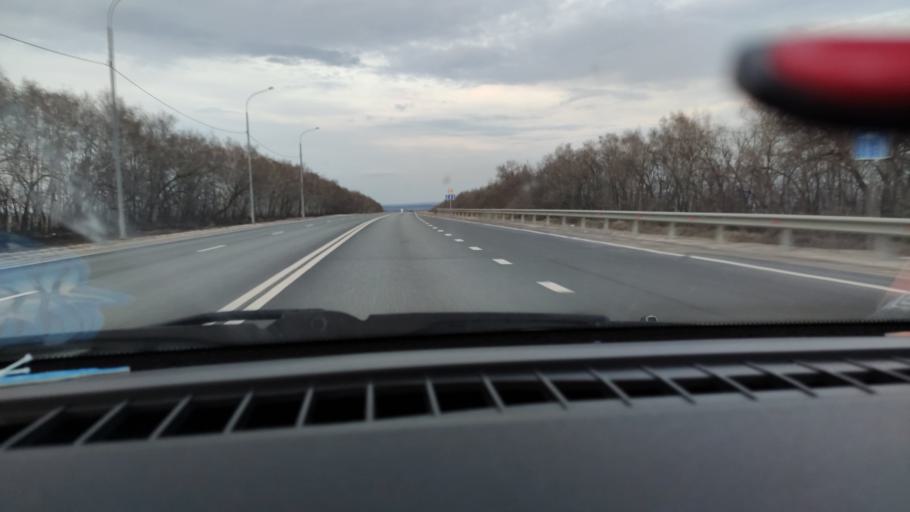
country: RU
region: Saratov
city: Sinodskoye
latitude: 51.9004
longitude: 46.5410
